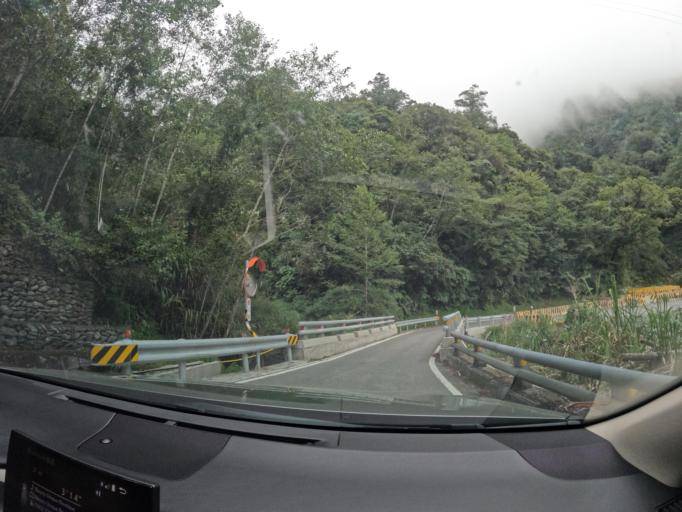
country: TW
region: Taiwan
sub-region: Taitung
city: Taitung
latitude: 23.2474
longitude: 120.9904
